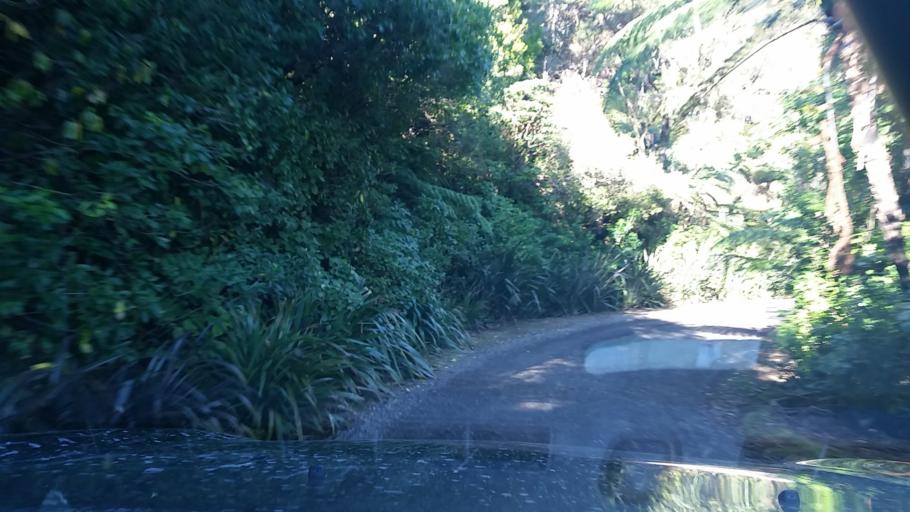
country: NZ
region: Marlborough
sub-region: Marlborough District
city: Picton
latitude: -41.1783
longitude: 173.9740
